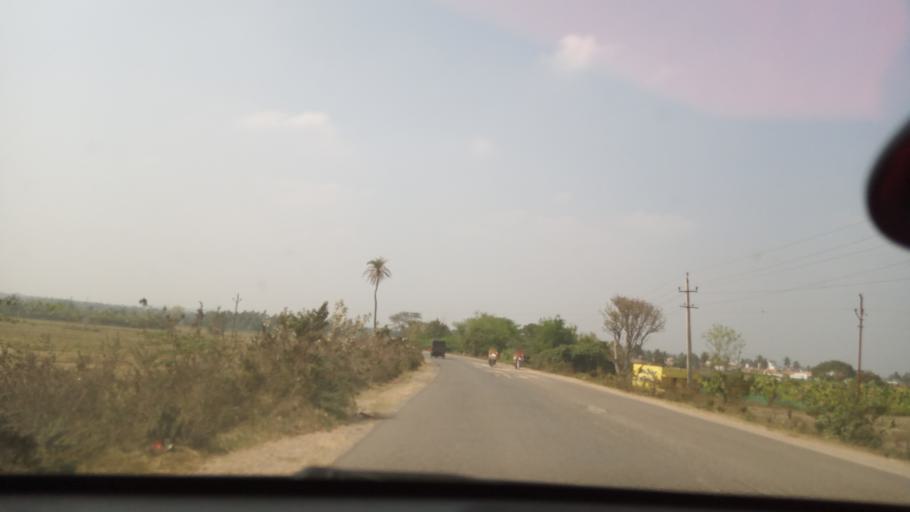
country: IN
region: Karnataka
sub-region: Mysore
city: Nanjangud
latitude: 12.1081
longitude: 76.7062
